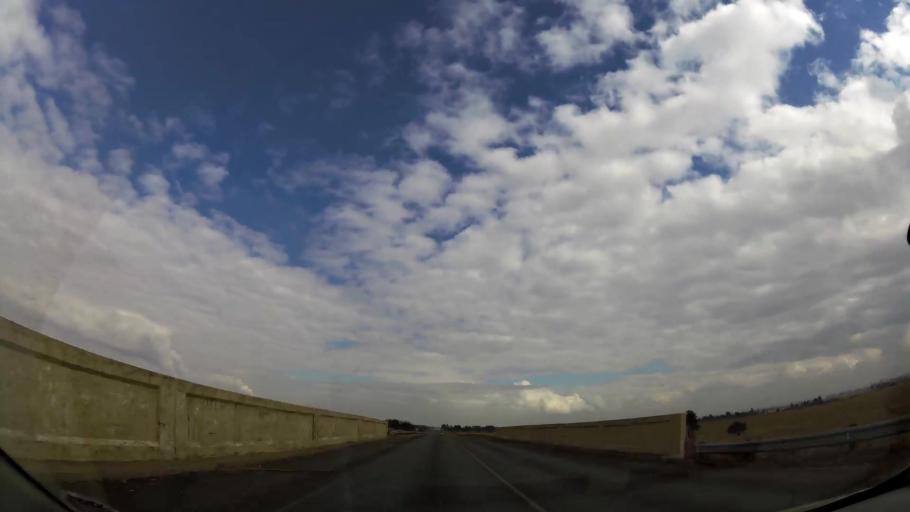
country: ZA
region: Gauteng
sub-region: Sedibeng District Municipality
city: Meyerton
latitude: -26.6358
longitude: 28.0599
